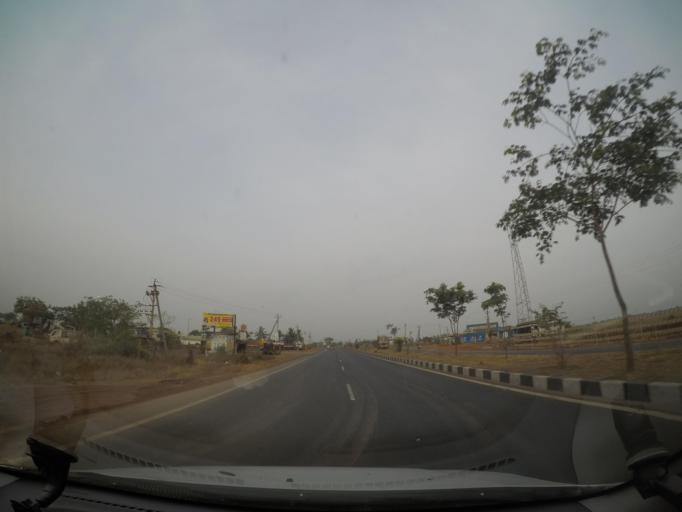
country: IN
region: Andhra Pradesh
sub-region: Krishna
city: Gannavaram
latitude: 16.6282
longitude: 80.9435
